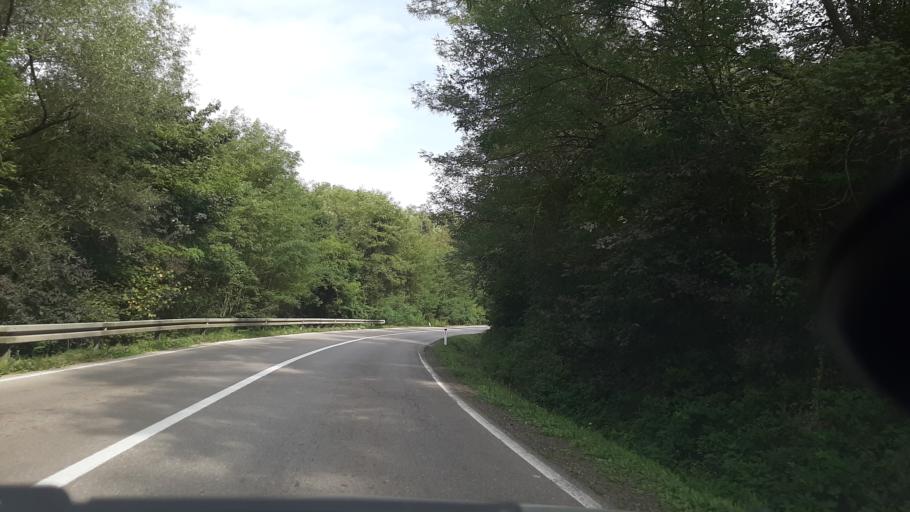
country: BA
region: Republika Srpska
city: Laktasi
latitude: 44.8763
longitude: 17.3621
